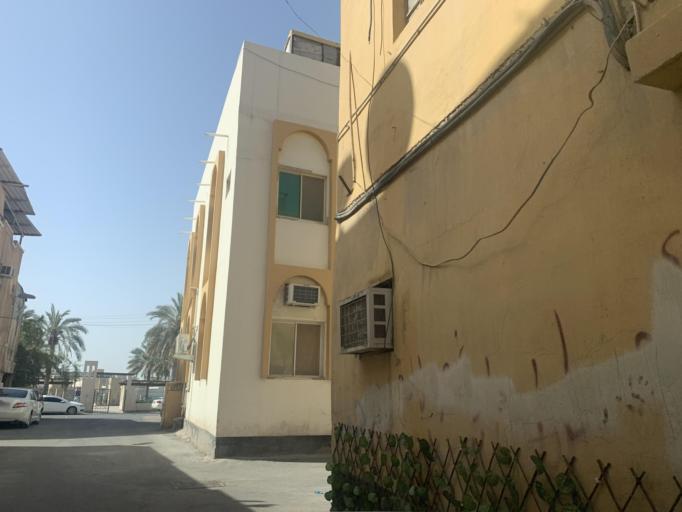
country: BH
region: Manama
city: Jidd Hafs
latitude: 26.2069
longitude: 50.5539
